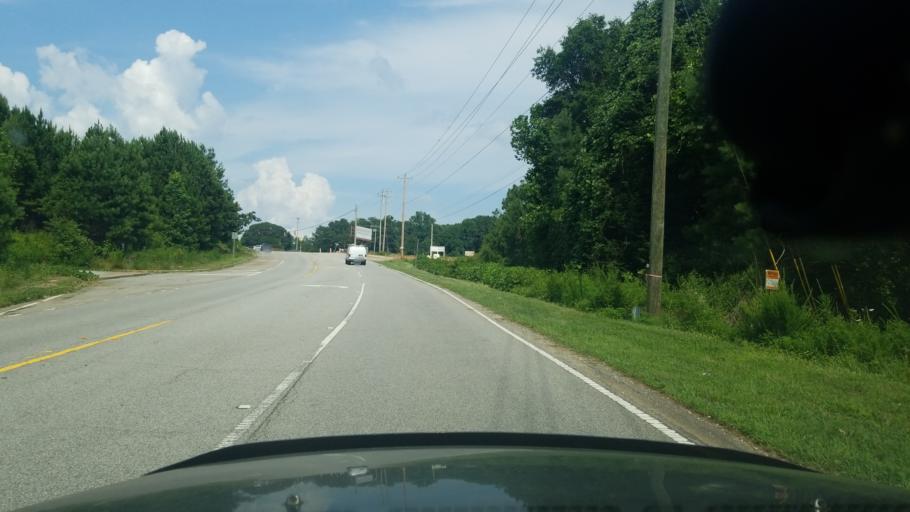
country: US
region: Georgia
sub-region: Dawson County
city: Dawsonville
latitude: 34.3117
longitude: -84.0681
